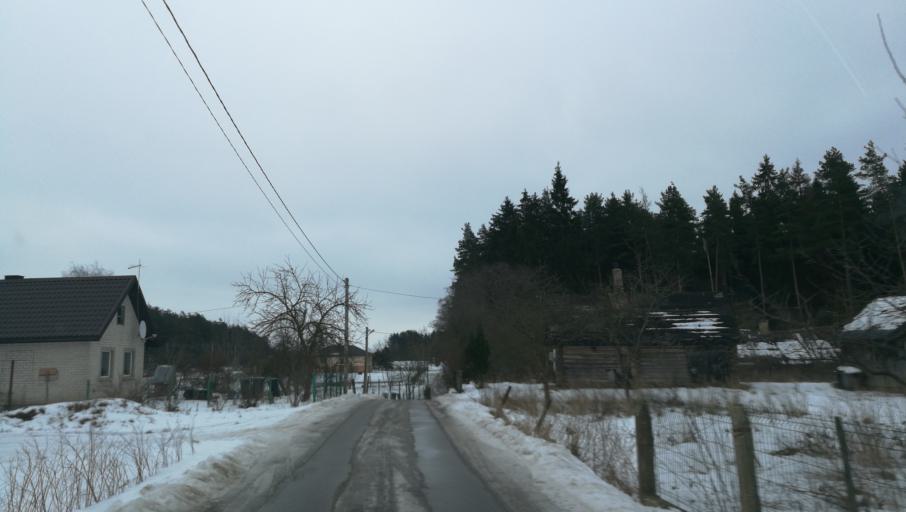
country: LT
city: Trakai
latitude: 54.6190
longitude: 24.9057
